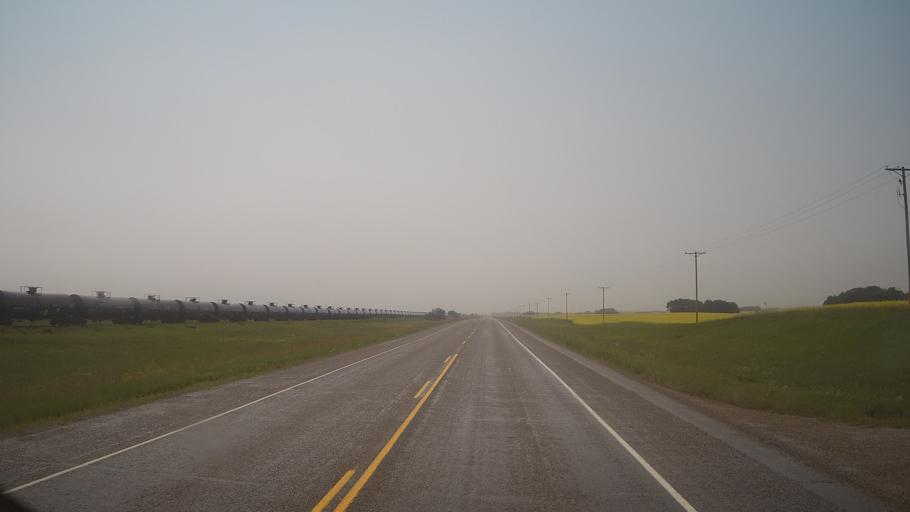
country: CA
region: Saskatchewan
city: Biggar
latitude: 52.1577
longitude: -108.2645
